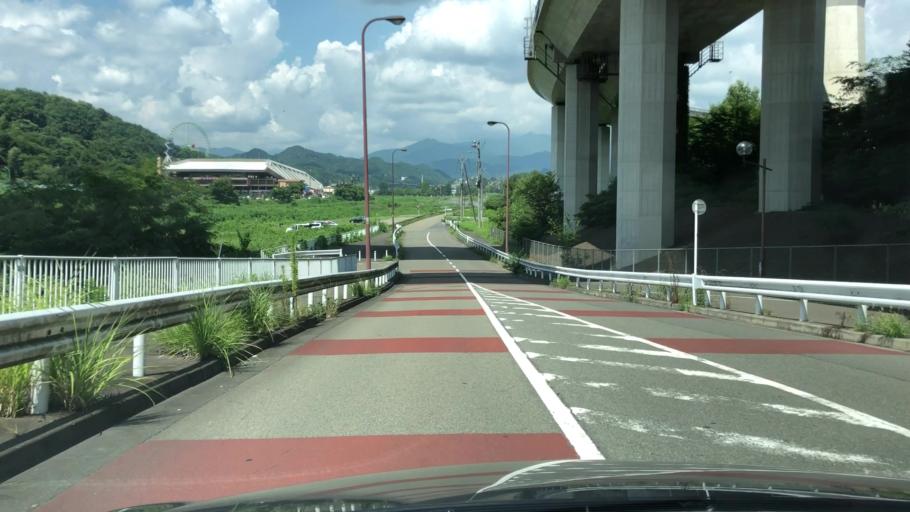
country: JP
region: Tokyo
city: Fussa
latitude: 35.7173
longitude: 139.2840
